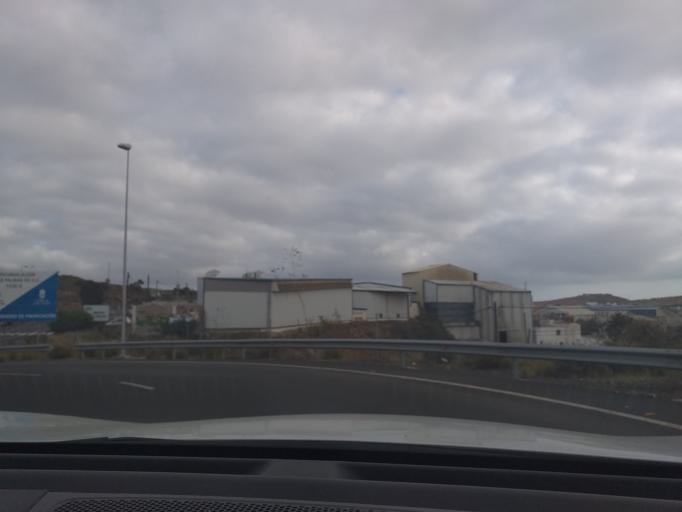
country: ES
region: Canary Islands
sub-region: Provincia de Las Palmas
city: Arucas
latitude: 28.1071
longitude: -15.4888
